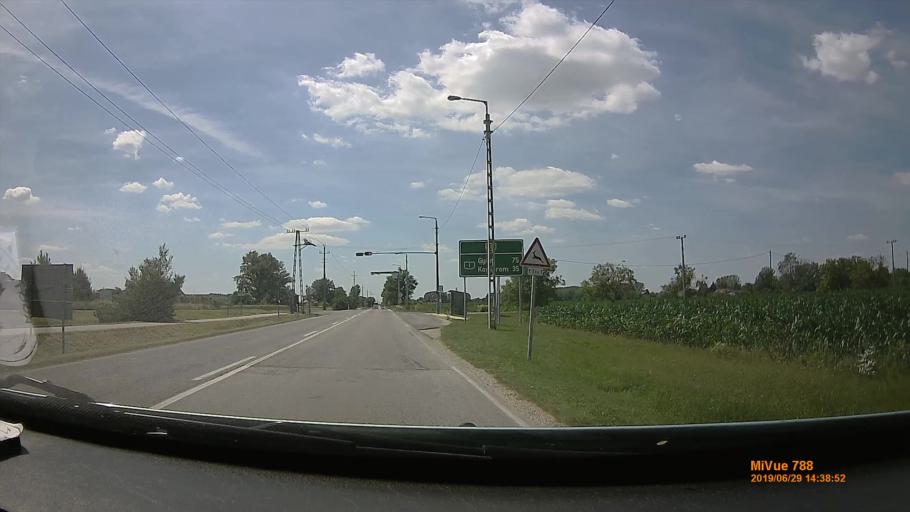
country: HU
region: Komarom-Esztergom
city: Tat
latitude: 47.7524
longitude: 18.6132
